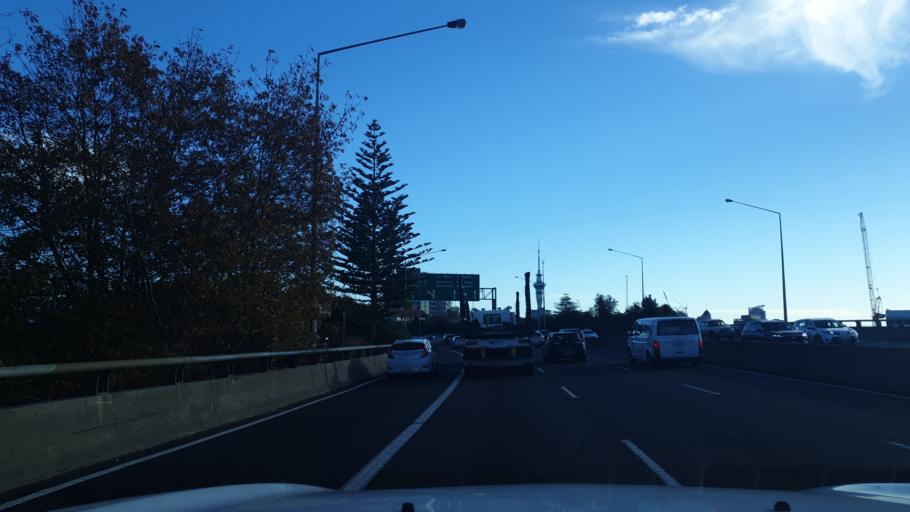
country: NZ
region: Auckland
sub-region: Auckland
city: Auckland
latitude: -36.8658
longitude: 174.7672
